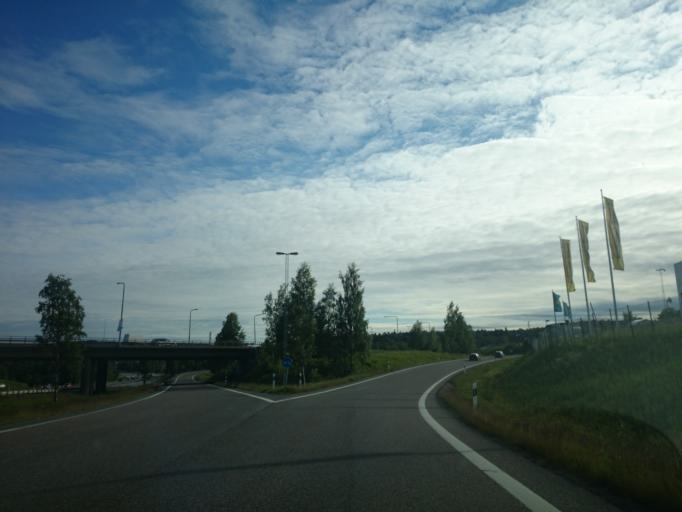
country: SE
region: Vaesternorrland
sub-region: Sundsvalls Kommun
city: Johannedal
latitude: 62.4135
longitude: 17.3409
